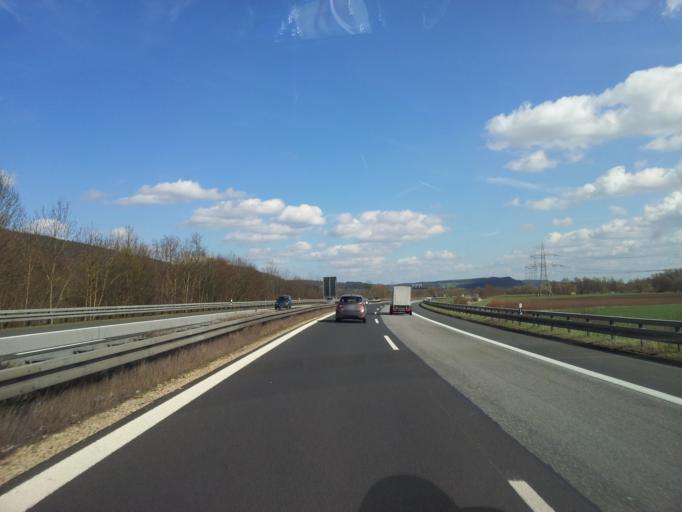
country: DE
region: Bavaria
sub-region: Regierungsbezirk Unterfranken
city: Ebelsbach
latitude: 49.9778
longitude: 10.6826
